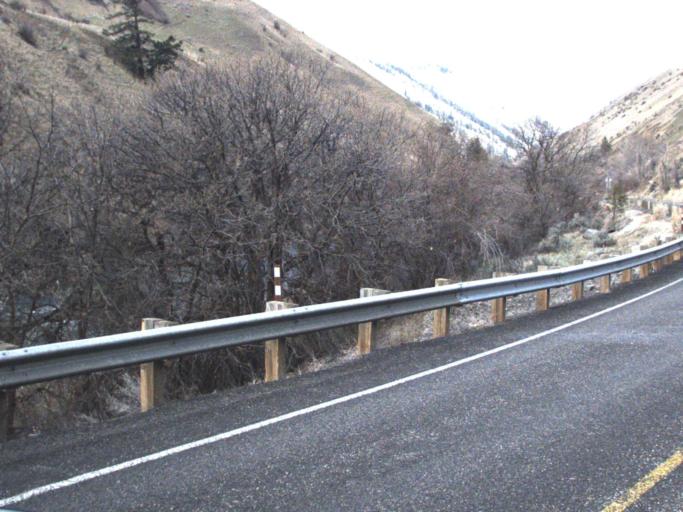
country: US
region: Washington
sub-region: Yakima County
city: Tieton
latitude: 46.7646
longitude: -120.8280
